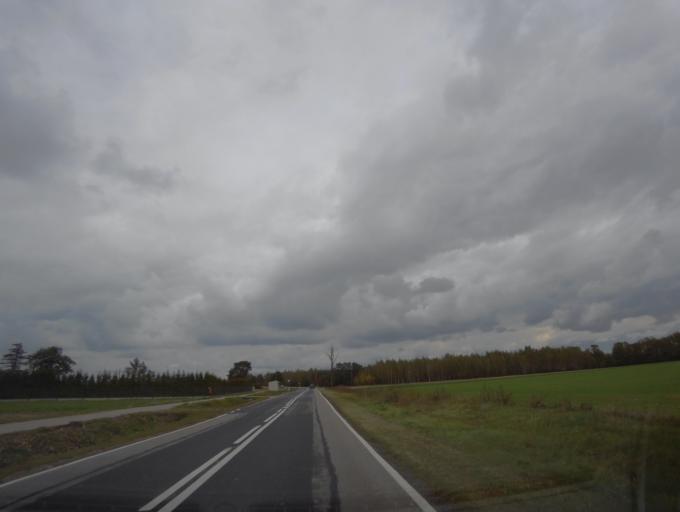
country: PL
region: Lublin Voivodeship
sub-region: Powiat wlodawski
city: Wlodawa
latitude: 51.6459
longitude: 23.5256
